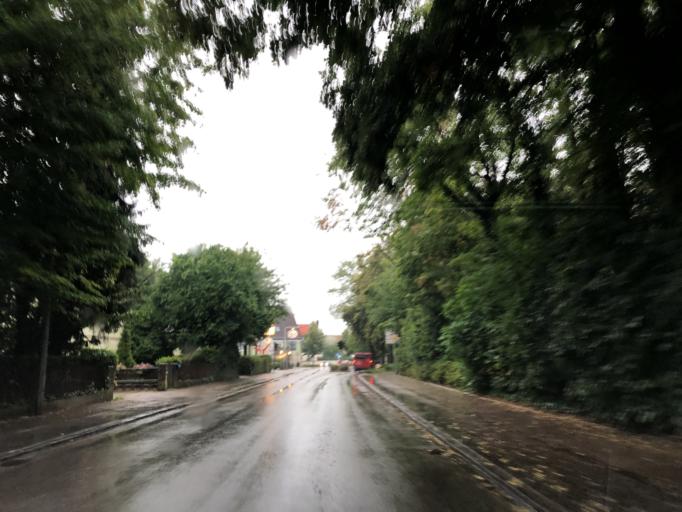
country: DE
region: Bavaria
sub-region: Upper Bavaria
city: Erding
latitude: 48.2975
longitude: 11.8998
